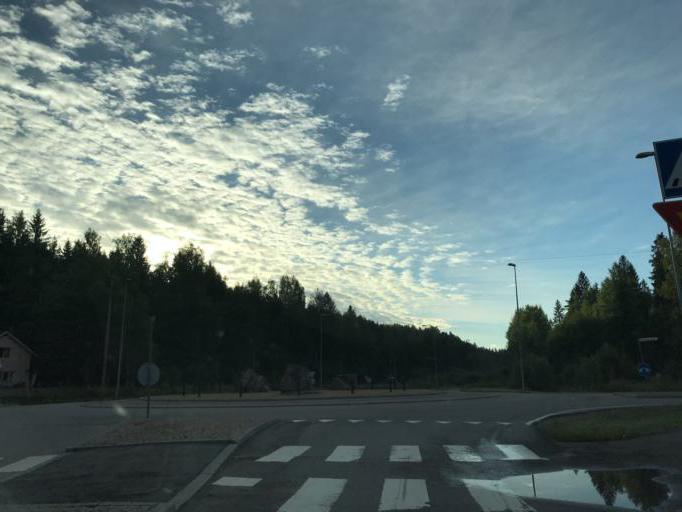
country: FI
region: Uusimaa
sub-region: Helsinki
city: Vihti
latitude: 60.4026
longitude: 24.4928
